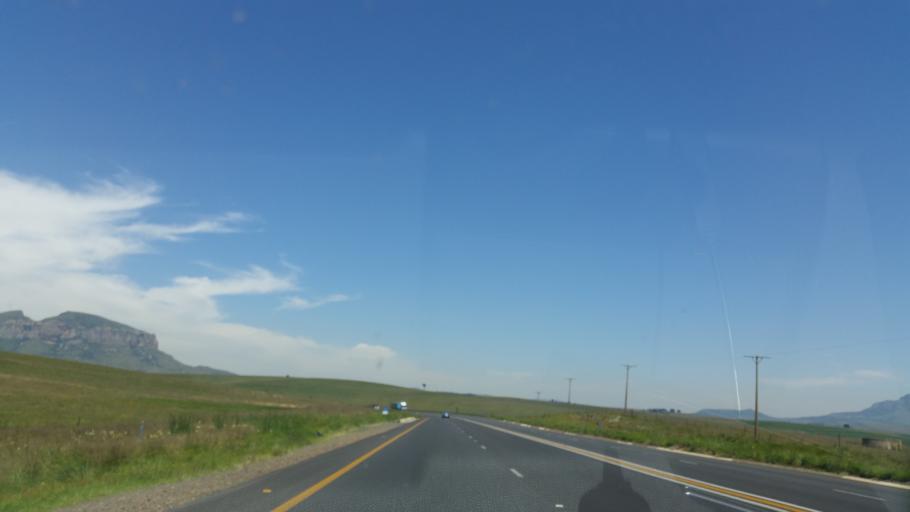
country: ZA
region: Orange Free State
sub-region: Thabo Mofutsanyana District Municipality
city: Harrismith
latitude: -28.3665
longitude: 29.3446
